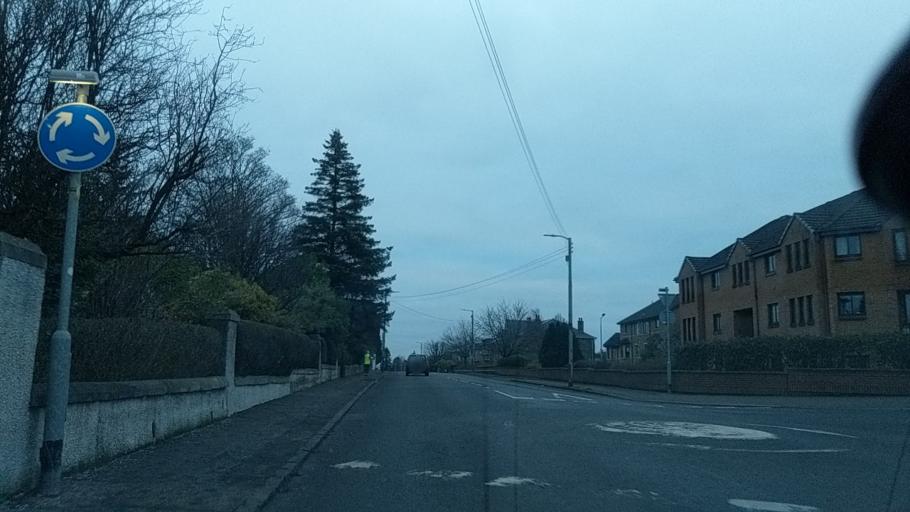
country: GB
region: Scotland
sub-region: South Lanarkshire
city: Rutherglen
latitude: 55.8158
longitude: -4.1878
